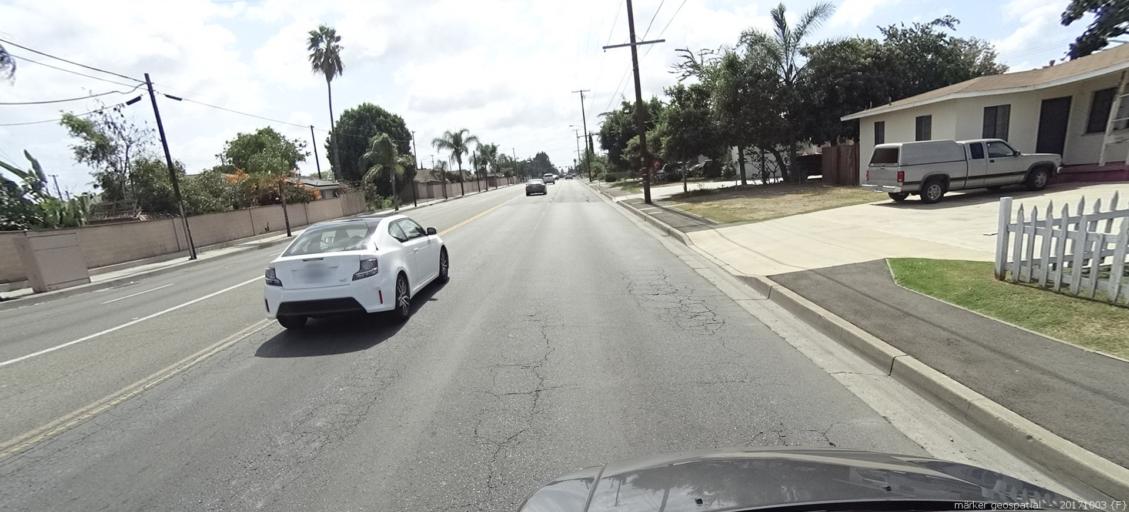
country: US
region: California
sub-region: Orange County
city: Garden Grove
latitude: 33.7707
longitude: -117.9030
